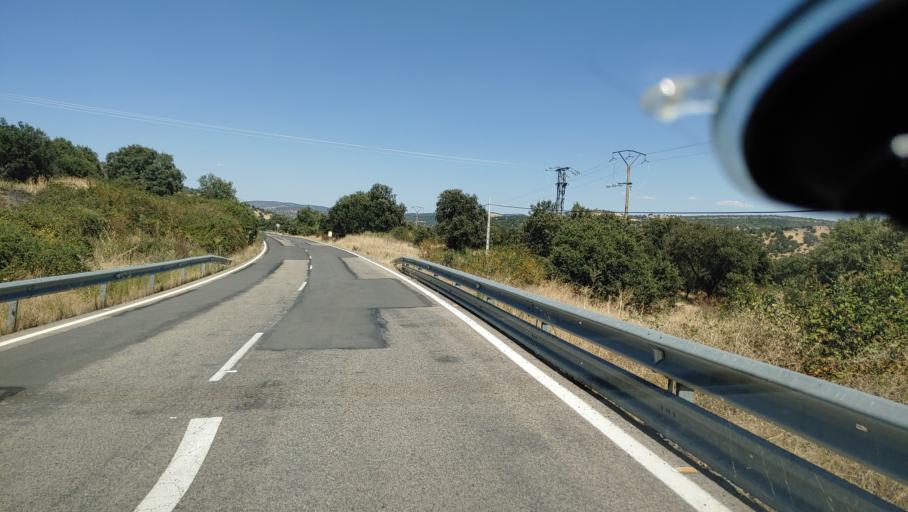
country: ES
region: Castille-La Mancha
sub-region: Provincia de Ciudad Real
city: Alamillo
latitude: 38.7464
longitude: -4.7003
